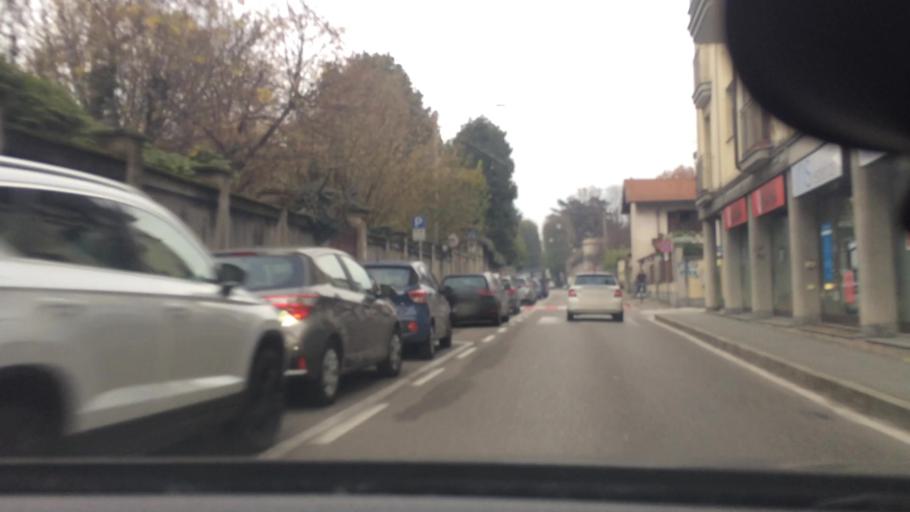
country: IT
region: Lombardy
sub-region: Provincia di Varese
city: Saronno
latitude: 45.6238
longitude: 9.0435
